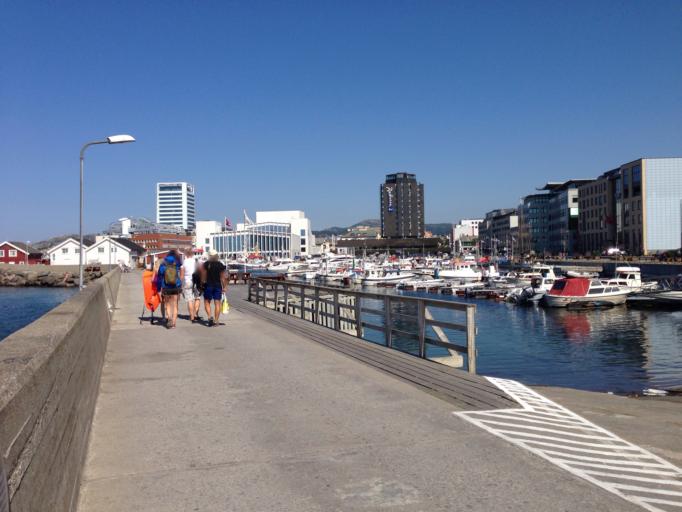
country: NO
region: Nordland
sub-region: Bodo
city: Bodo
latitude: 67.2804
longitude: 14.3690
